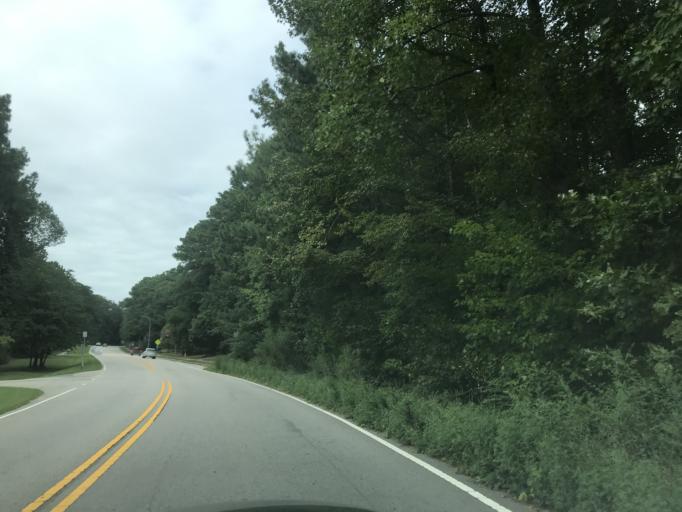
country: US
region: North Carolina
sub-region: Wake County
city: Apex
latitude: 35.7464
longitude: -78.8161
